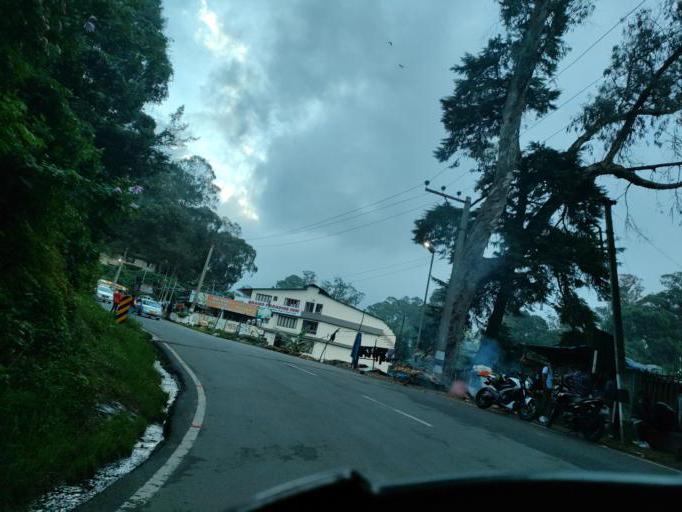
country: IN
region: Tamil Nadu
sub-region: Dindigul
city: Kodaikanal
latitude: 10.2383
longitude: 77.4929
